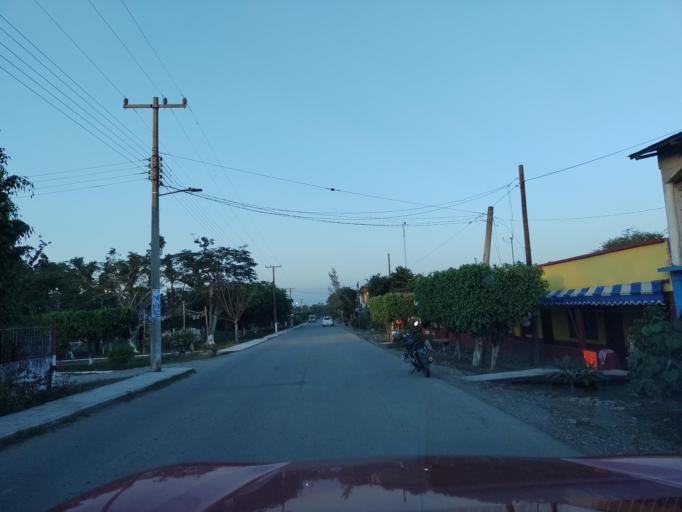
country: MX
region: Veracruz
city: Agua Dulce
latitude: 20.3149
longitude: -97.2722
